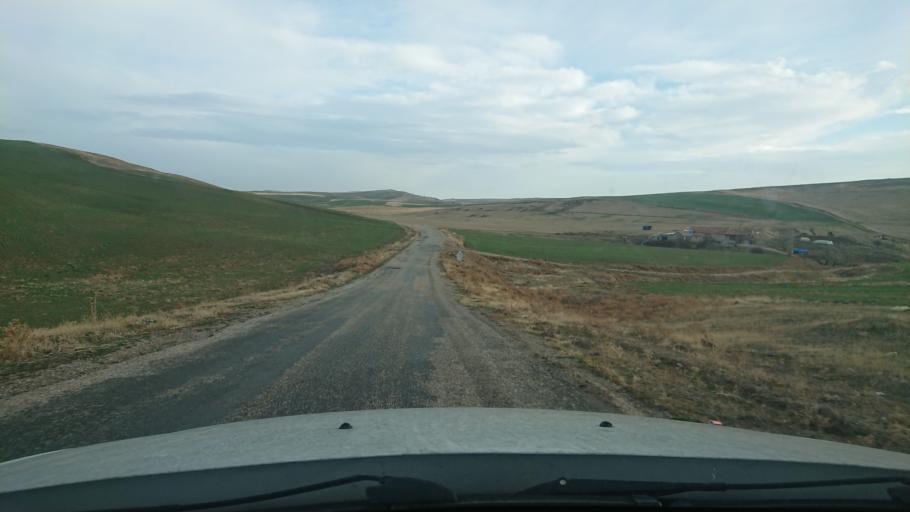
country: TR
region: Aksaray
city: Acipinar
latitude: 38.6375
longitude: 33.8049
